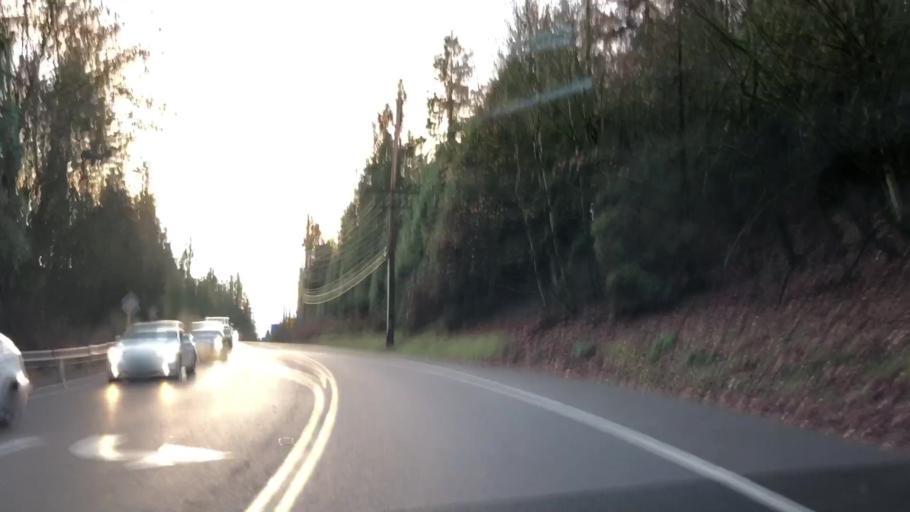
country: US
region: Washington
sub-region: King County
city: Sammamish
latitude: 47.6443
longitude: -122.0566
